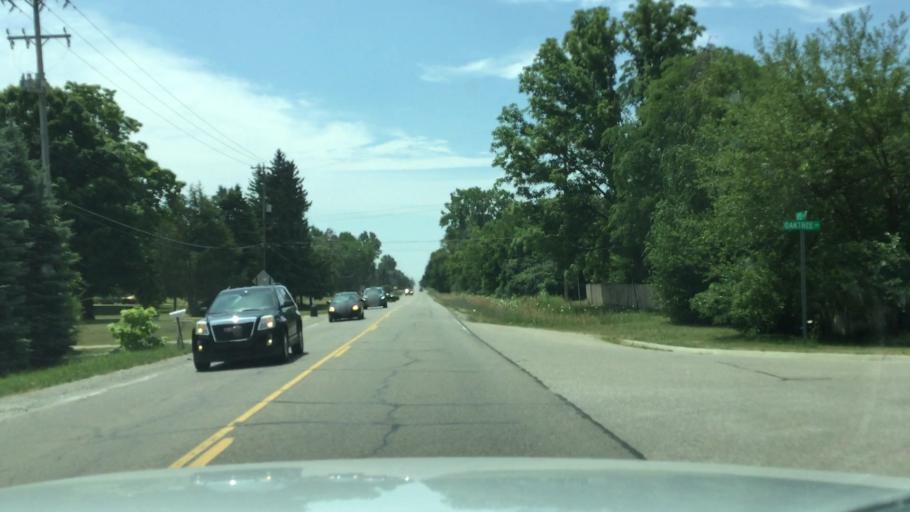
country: US
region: Michigan
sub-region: Genesee County
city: Swartz Creek
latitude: 43.0153
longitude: -83.7830
